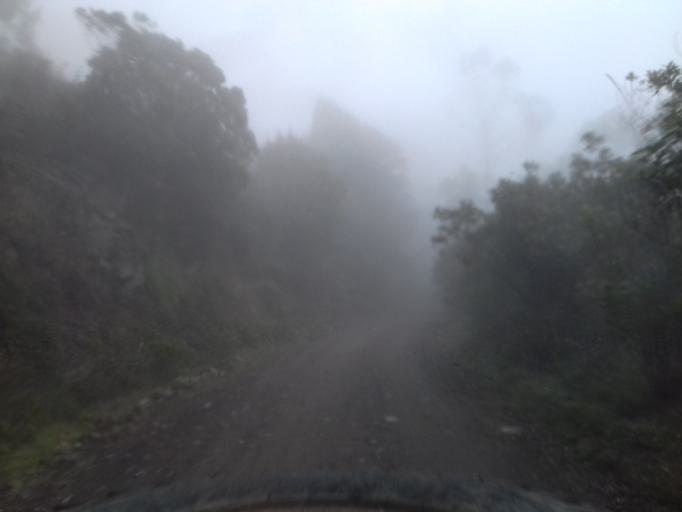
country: CO
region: Tolima
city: Murillo
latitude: 4.9034
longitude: -75.2514
